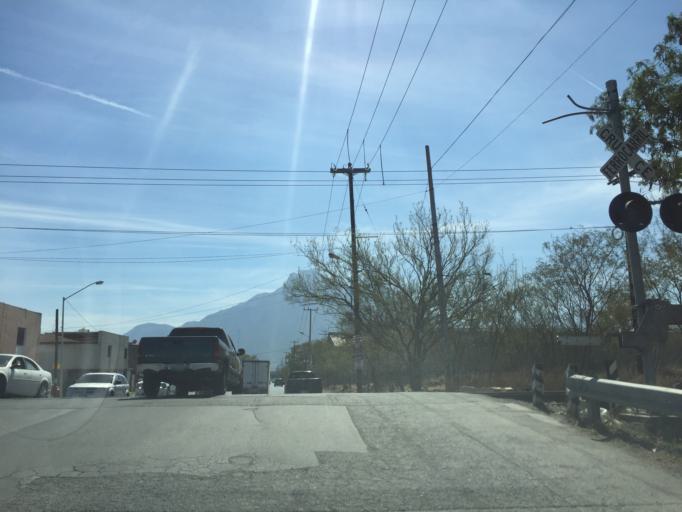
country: MX
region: Nuevo Leon
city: Guadalupe
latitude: 25.6989
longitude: -100.2400
